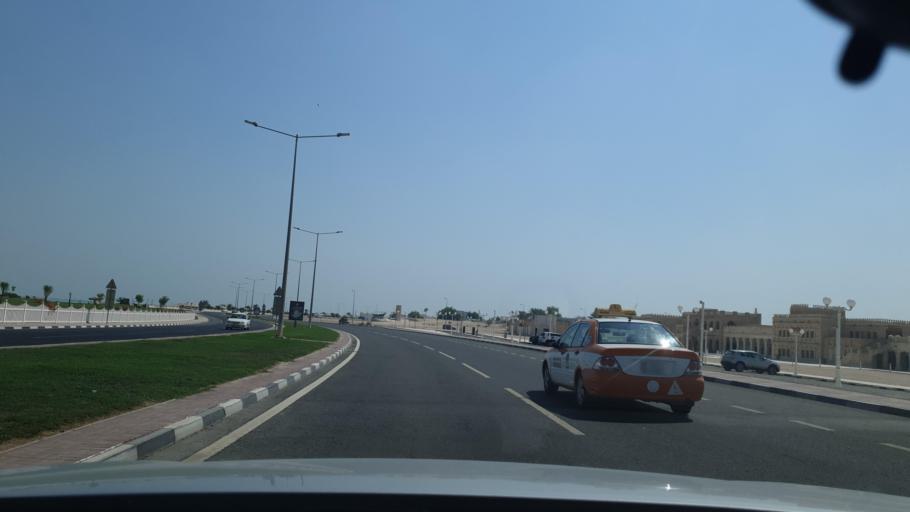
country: QA
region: Al Khawr
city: Al Khawr
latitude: 25.6899
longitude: 51.5016
